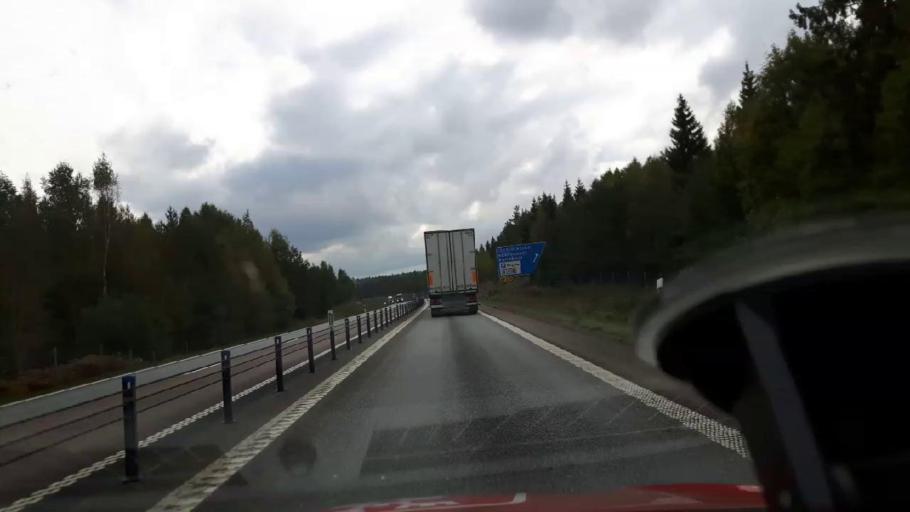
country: SE
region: Gaevleborg
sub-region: Gavle Kommun
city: Norrsundet
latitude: 60.9084
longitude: 17.0145
